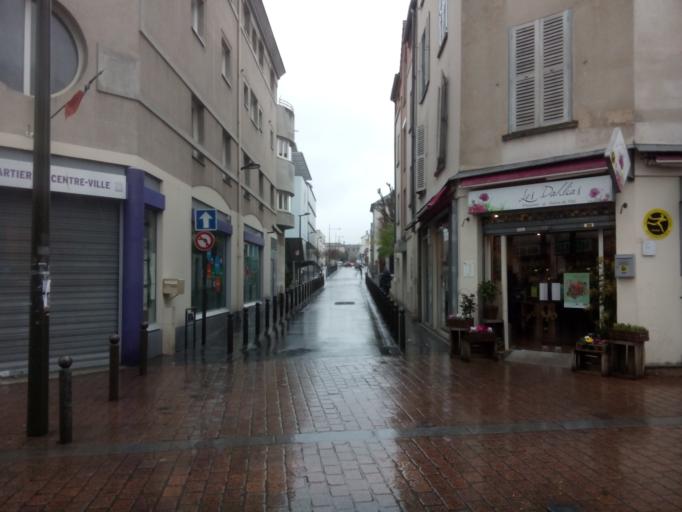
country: FR
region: Ile-de-France
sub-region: Departement du Val-d'Oise
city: Argenteuil
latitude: 48.9430
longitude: 2.2483
